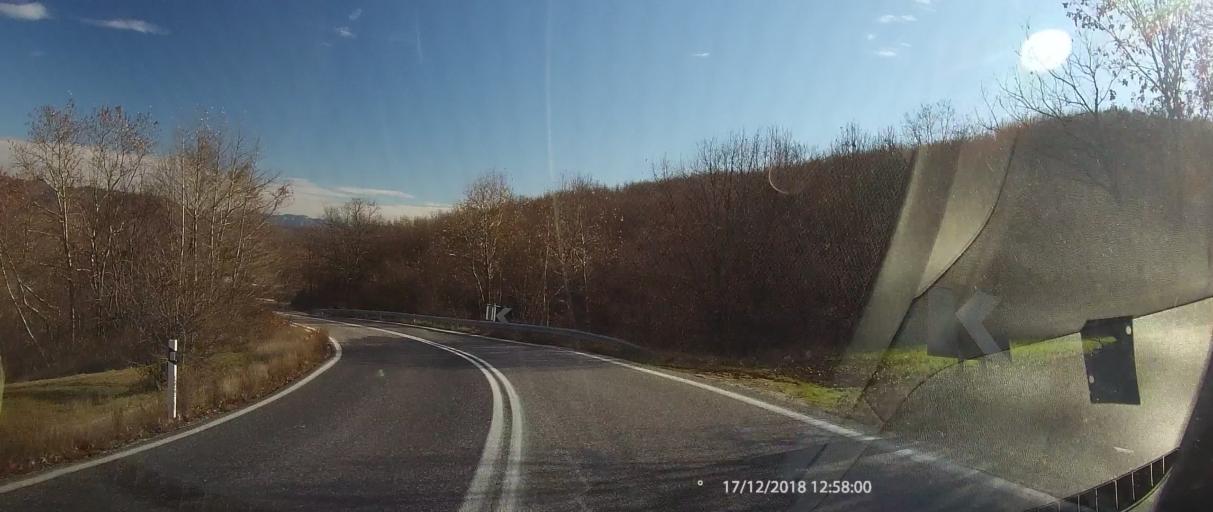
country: GR
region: Thessaly
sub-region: Trikala
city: Kastraki
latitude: 39.7423
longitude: 21.5364
